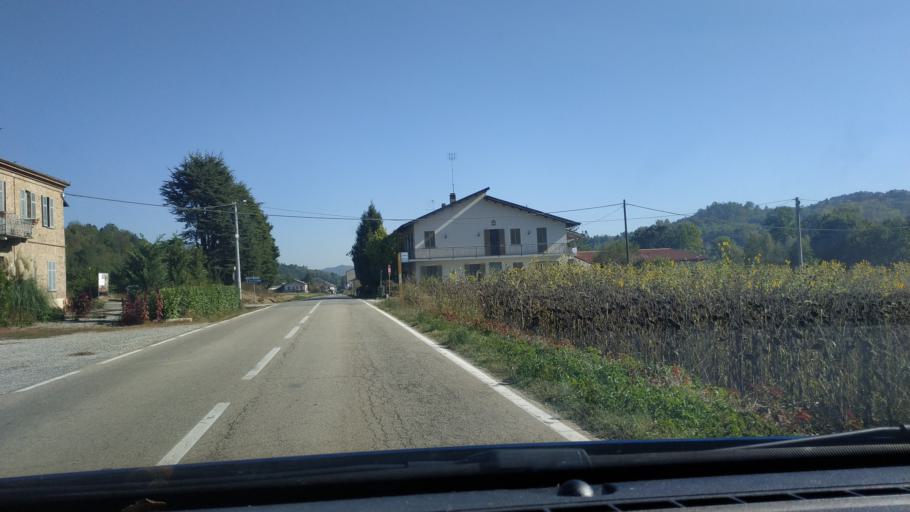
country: IT
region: Piedmont
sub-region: Provincia di Alessandria
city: Odalengo Grande
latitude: 45.1011
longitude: 8.1939
